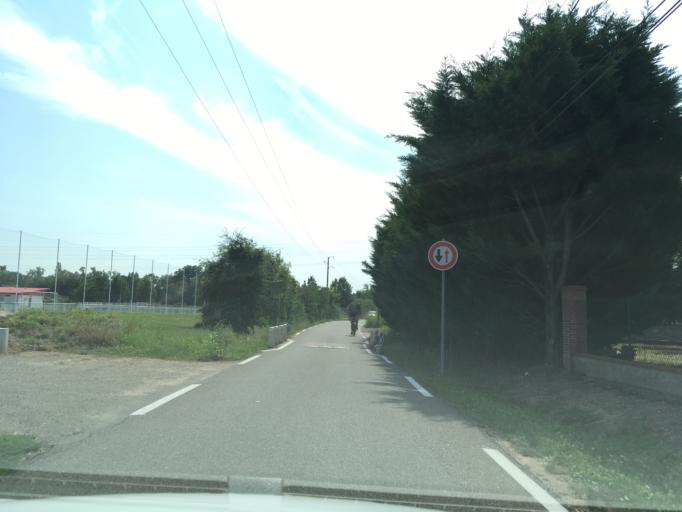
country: FR
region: Midi-Pyrenees
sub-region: Departement du Tarn-et-Garonne
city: Montauban
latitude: 44.0117
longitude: 1.3377
